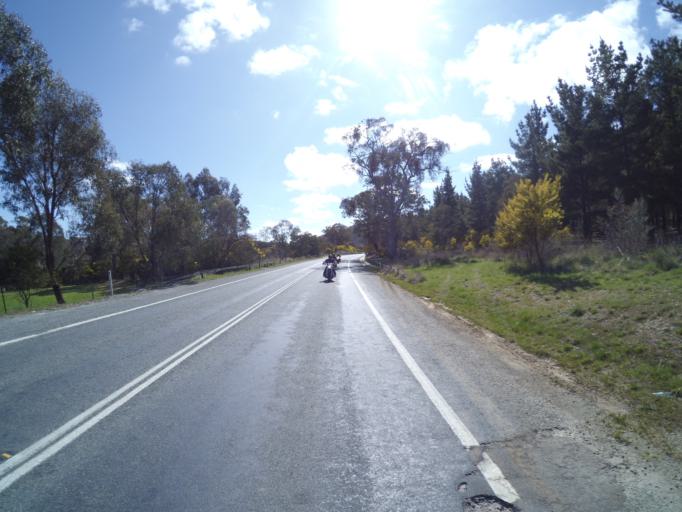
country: AU
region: New South Wales
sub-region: Queanbeyan
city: Queanbeyan
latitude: -35.2938
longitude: 149.2557
